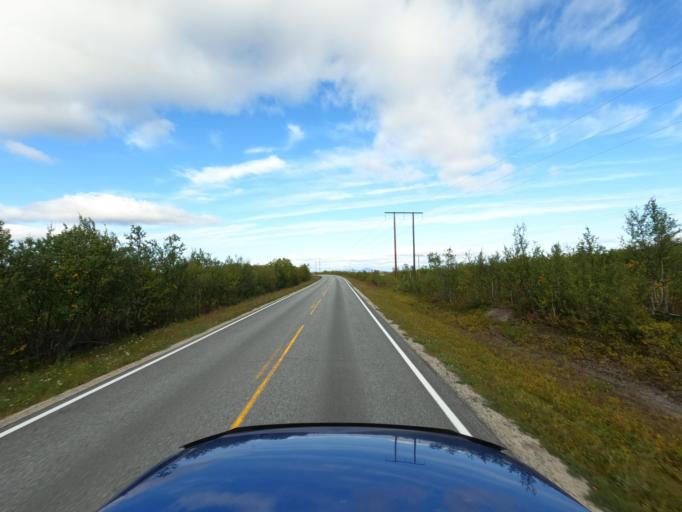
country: NO
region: Finnmark Fylke
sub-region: Karasjok
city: Karasjohka
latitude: 69.6630
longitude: 25.2763
